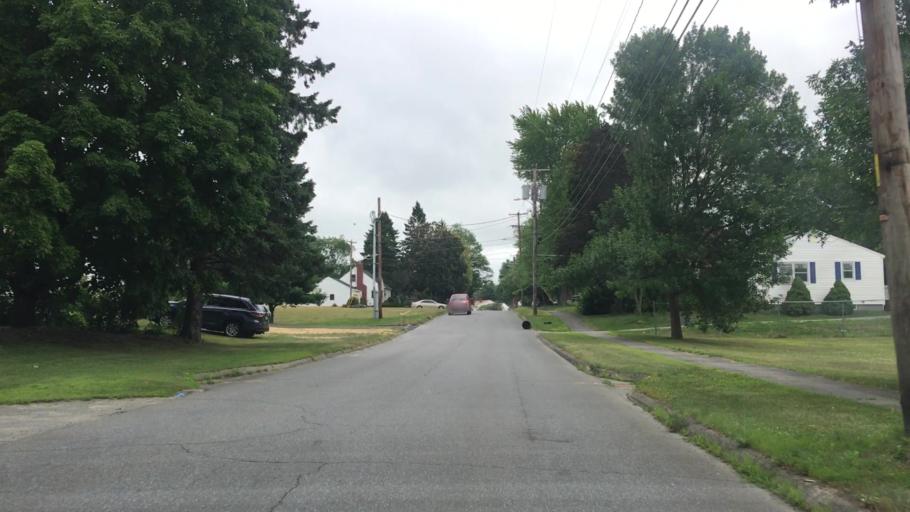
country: US
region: Maine
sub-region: Penobscot County
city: Brewer
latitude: 44.7873
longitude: -68.7513
